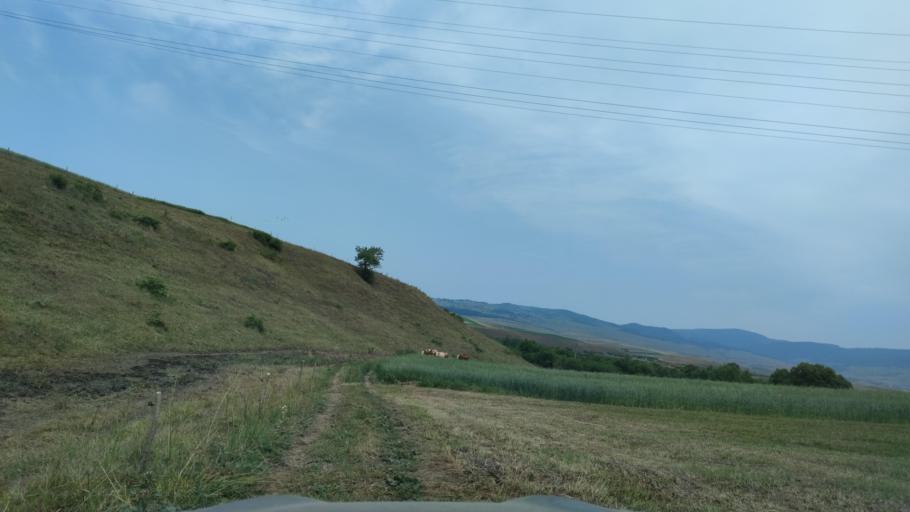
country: RO
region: Harghita
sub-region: Comuna Subcetate
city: Subcetate
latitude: 46.8242
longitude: 25.4503
